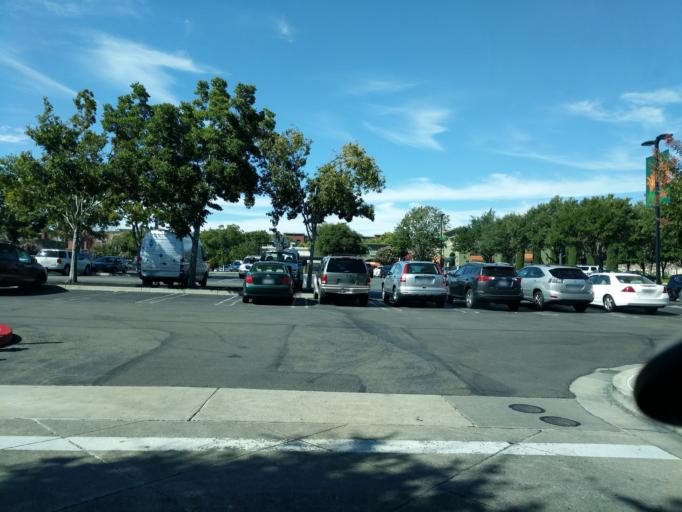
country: US
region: California
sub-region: Alameda County
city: Pleasanton
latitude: 37.7061
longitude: -121.8730
